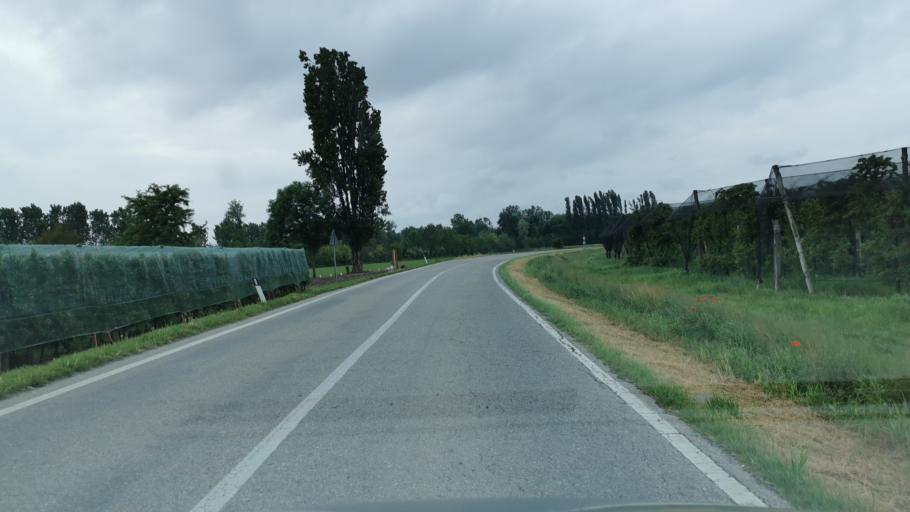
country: IT
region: Piedmont
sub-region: Provincia di Cuneo
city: Genola
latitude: 44.6136
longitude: 7.6253
